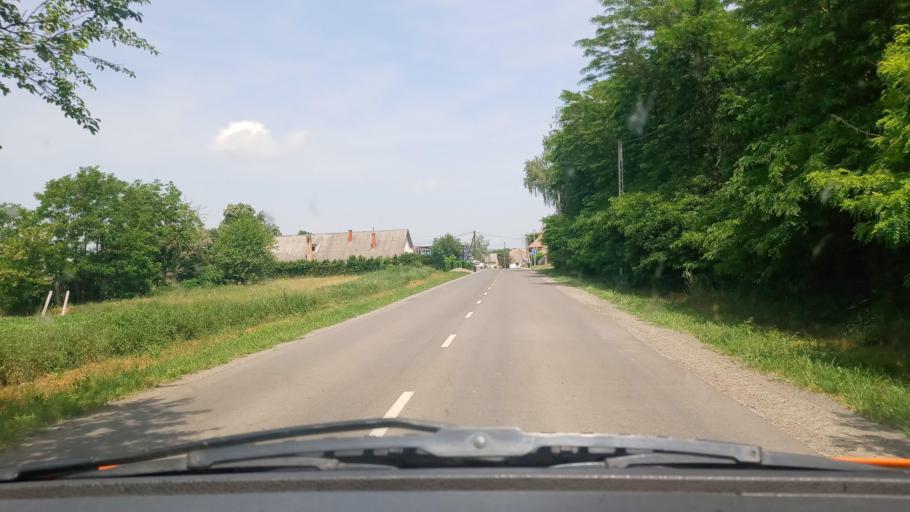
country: HU
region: Baranya
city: Szigetvar
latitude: 45.9723
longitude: 17.7211
